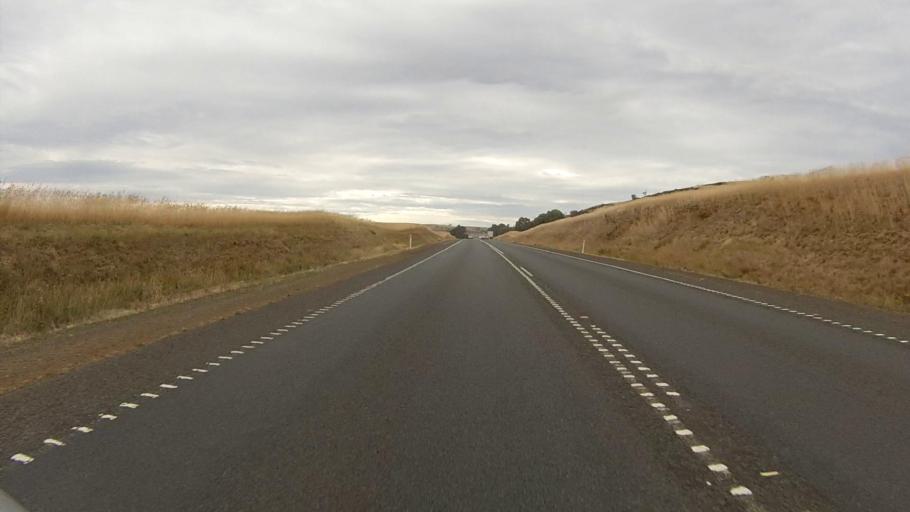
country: AU
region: Tasmania
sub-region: Brighton
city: Bridgewater
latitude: -42.3821
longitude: 147.3180
